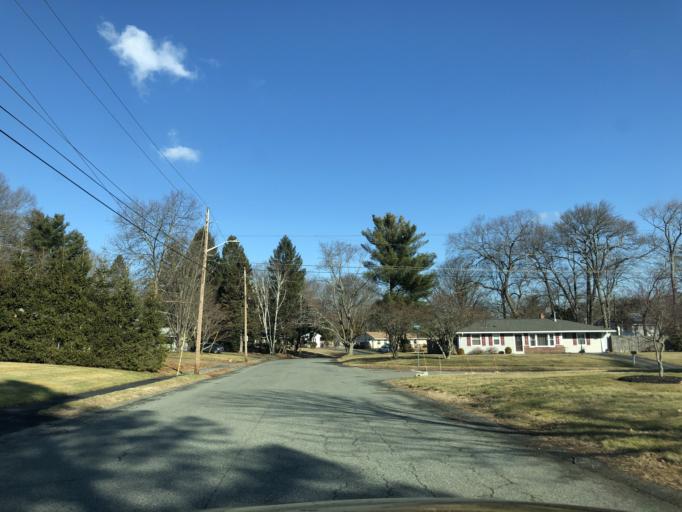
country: US
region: Massachusetts
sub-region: Plymouth County
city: Brockton
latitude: 42.1045
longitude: -71.0015
